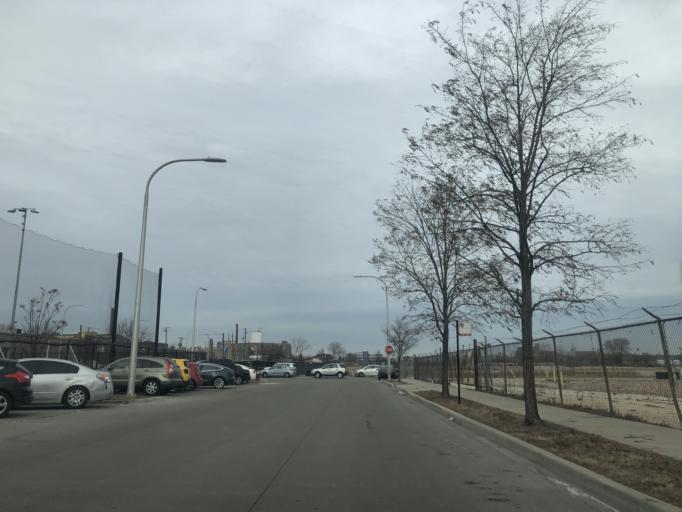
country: US
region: Illinois
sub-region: Cook County
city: Chicago
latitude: 41.9135
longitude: -87.6611
